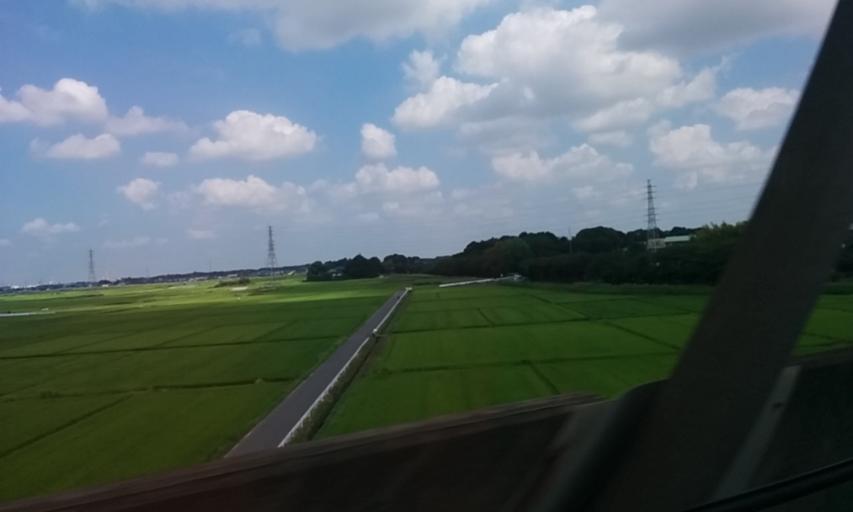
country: JP
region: Saitama
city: Shiraoka
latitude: 36.0015
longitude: 139.6402
